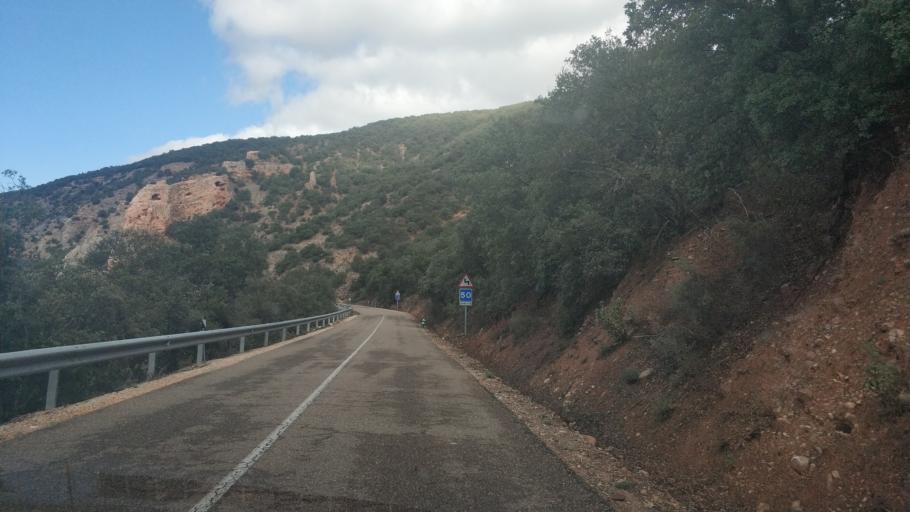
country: ES
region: Castille and Leon
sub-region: Provincia de Burgos
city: Retuerta
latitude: 42.0488
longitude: -3.4916
